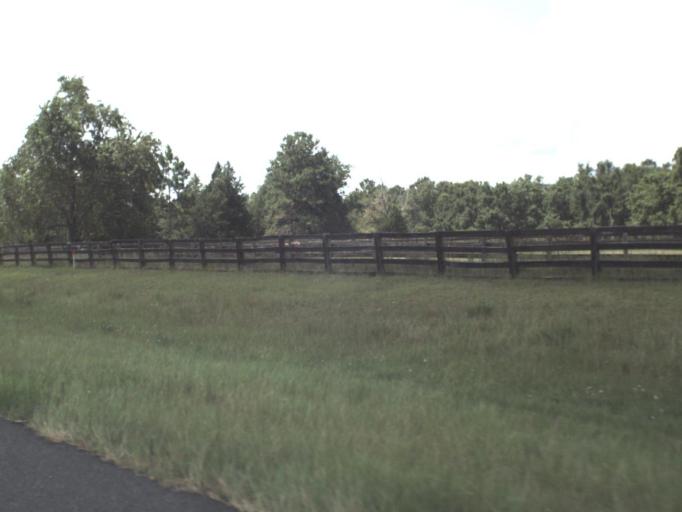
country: US
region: Florida
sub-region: Jefferson County
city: Monticello
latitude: 30.3151
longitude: -83.7590
